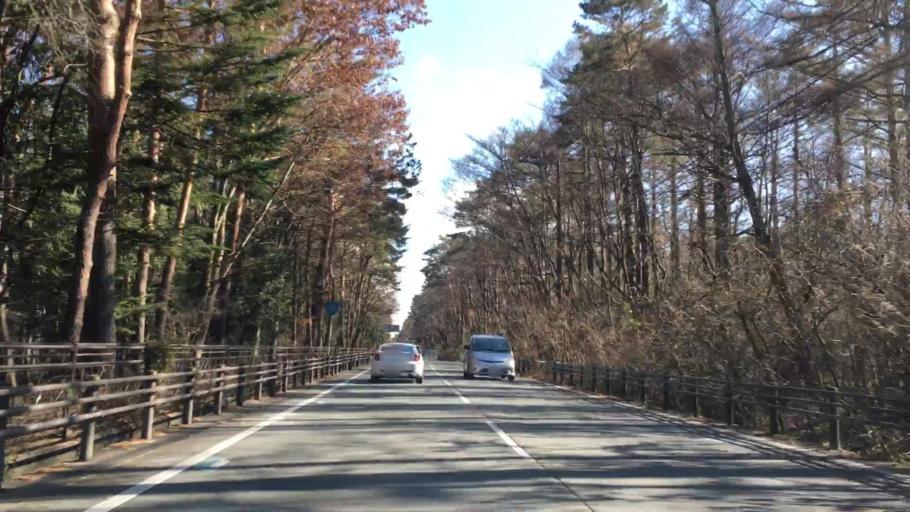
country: JP
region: Yamanashi
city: Fujikawaguchiko
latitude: 35.4490
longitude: 138.8177
